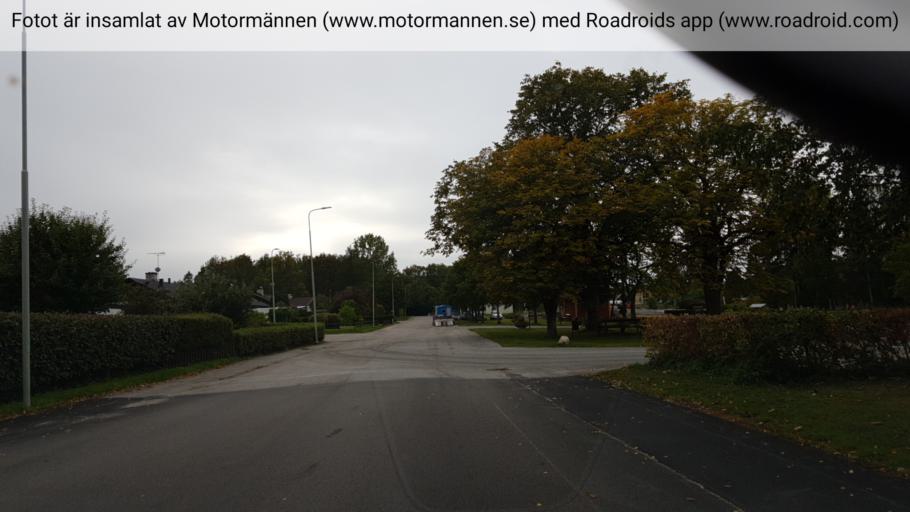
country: SE
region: Vaestra Goetaland
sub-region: Mariestads Kommun
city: Mariestad
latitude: 58.6443
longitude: 13.7028
